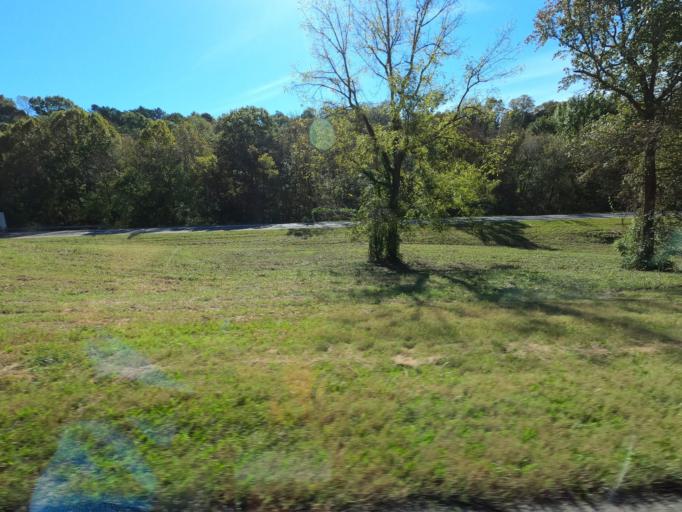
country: US
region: Tennessee
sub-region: Dickson County
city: White Bluff
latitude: 36.0264
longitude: -87.2185
